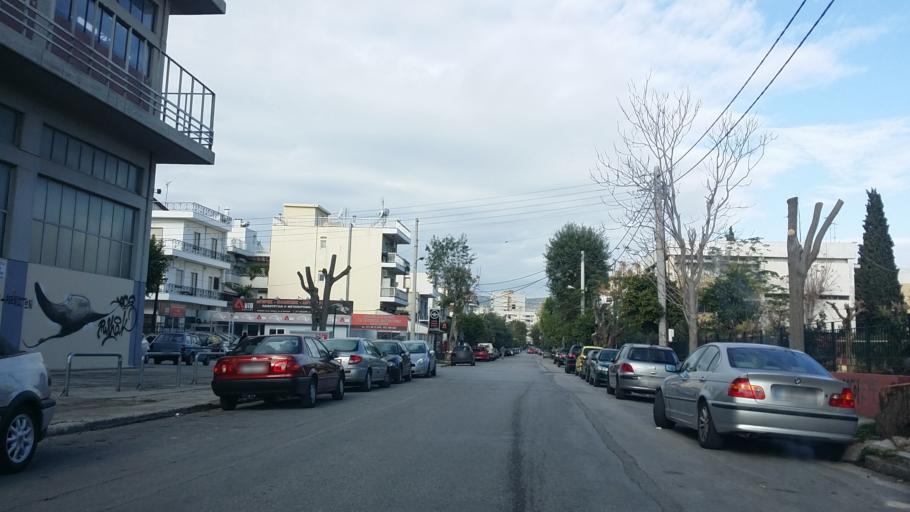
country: GR
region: Attica
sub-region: Nomarchia Athinas
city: Peristeri
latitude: 38.0033
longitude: 23.7046
